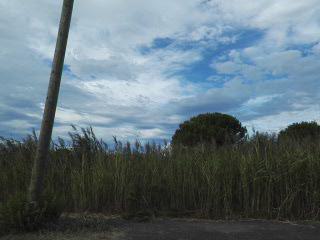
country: FR
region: Languedoc-Roussillon
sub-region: Departement de l'Herault
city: Le Cap d'Agde
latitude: 43.3131
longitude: 3.5401
